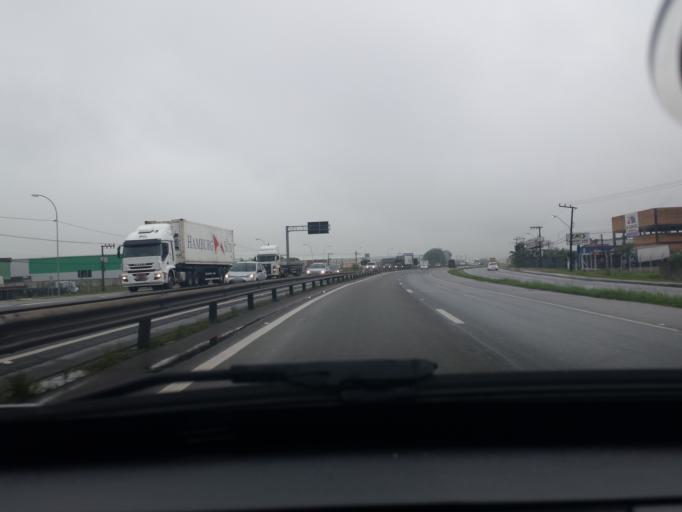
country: BR
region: Santa Catarina
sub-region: Itajai
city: Itajai
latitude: -26.8676
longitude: -48.7301
